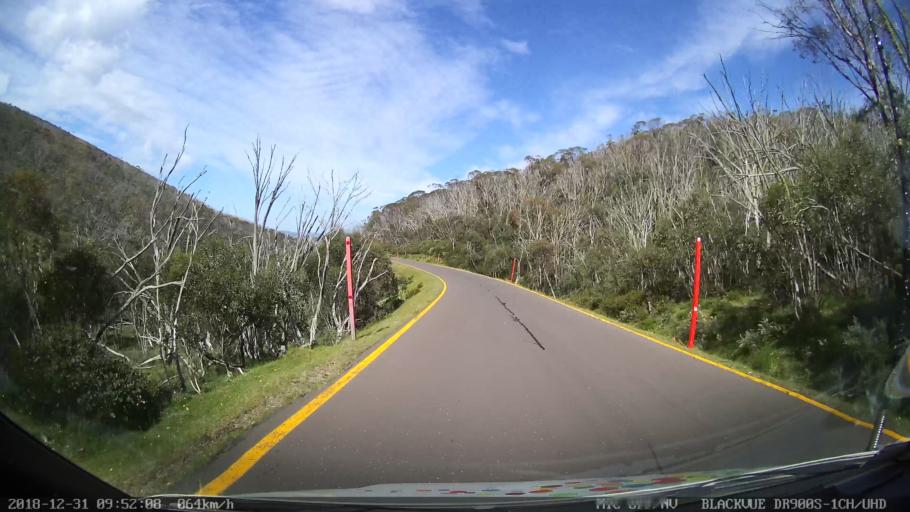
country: AU
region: New South Wales
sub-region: Snowy River
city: Jindabyne
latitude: -36.5256
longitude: 148.2563
